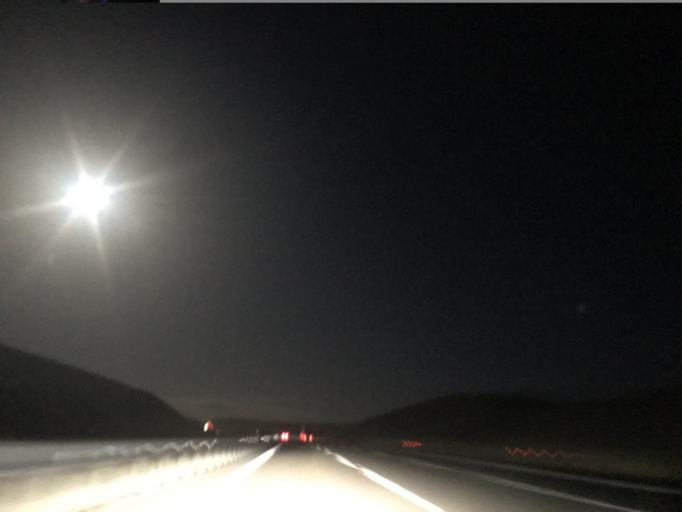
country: TR
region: Nigde
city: Ulukisla
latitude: 37.6416
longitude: 34.3800
